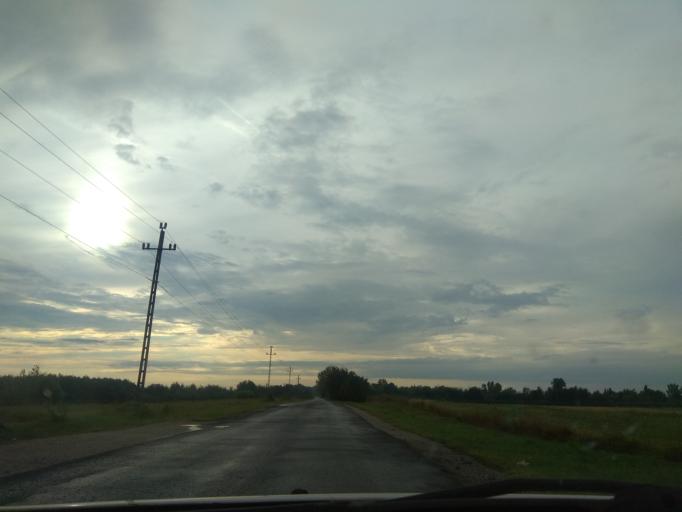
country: HU
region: Borsod-Abauj-Zemplen
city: Onga
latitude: 48.1169
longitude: 20.9347
